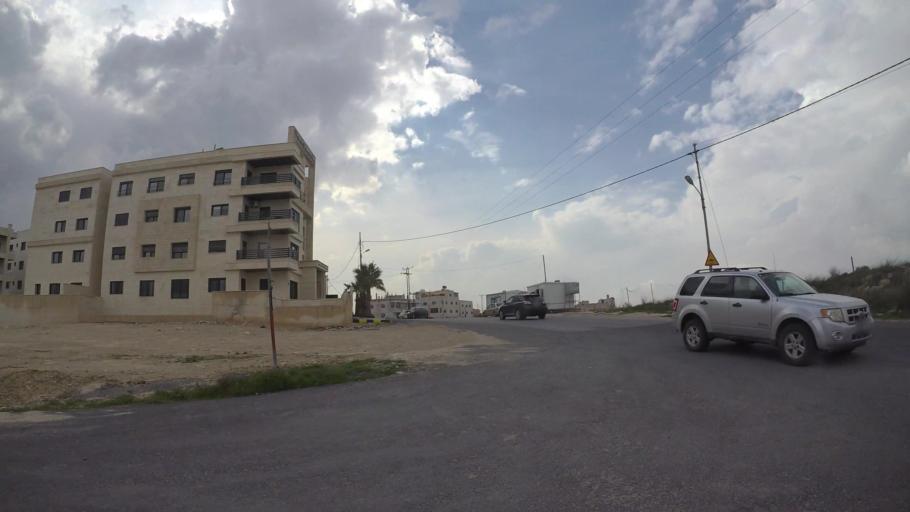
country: JO
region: Amman
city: Umm as Summaq
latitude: 31.8879
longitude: 35.8626
